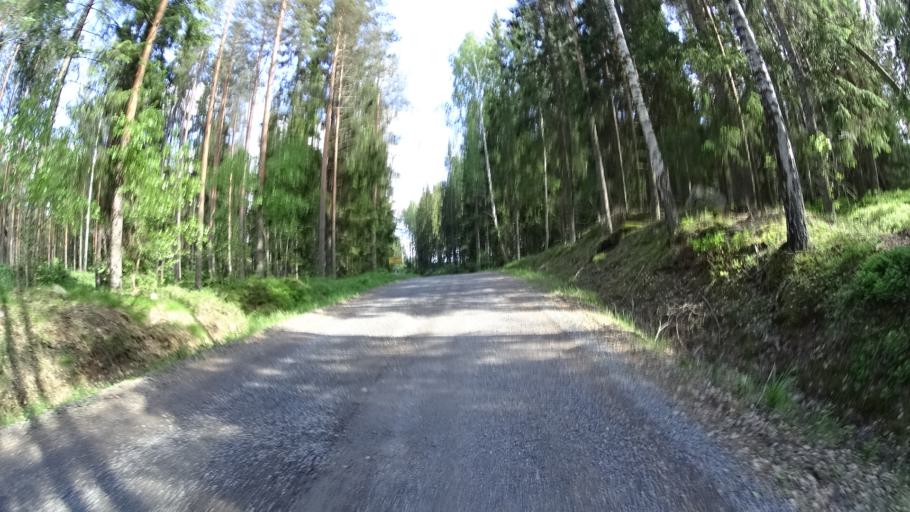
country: FI
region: Varsinais-Suomi
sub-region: Salo
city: Kisko
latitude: 60.1928
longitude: 23.5531
